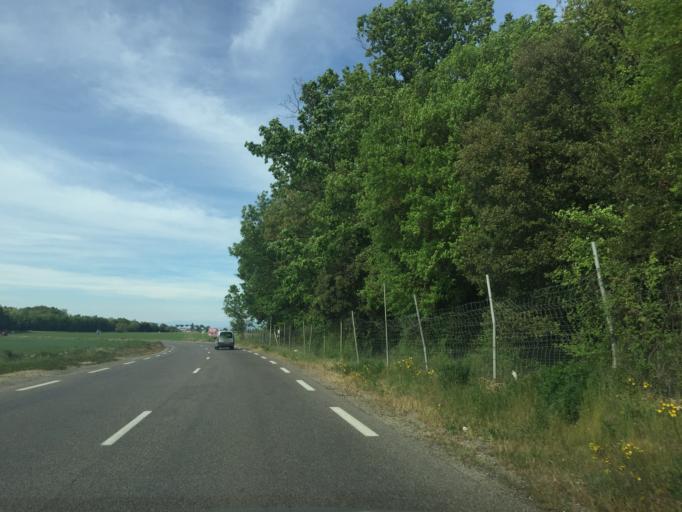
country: FR
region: Provence-Alpes-Cote d'Azur
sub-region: Departement des Alpes-de-Haute-Provence
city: Sainte-Tulle
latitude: 43.7805
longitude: 5.8209
